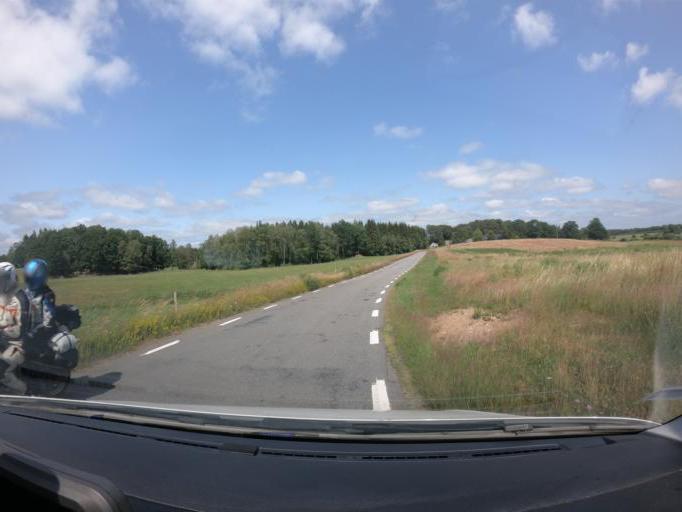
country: SE
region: Skane
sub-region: Hassleholms Kommun
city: Sosdala
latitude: 55.9476
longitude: 13.6412
